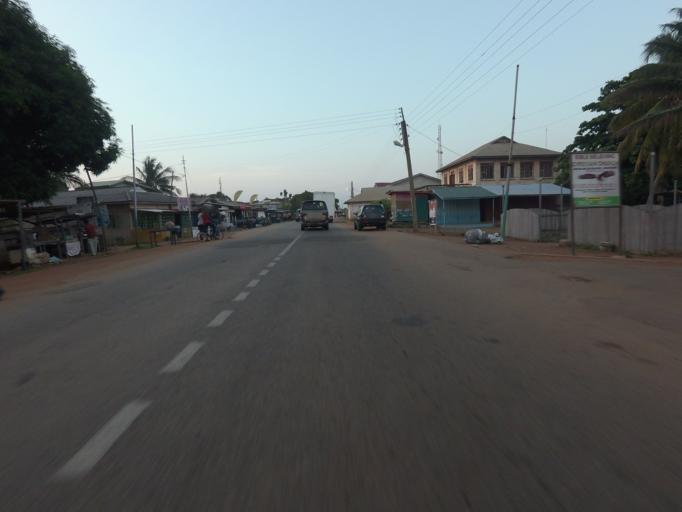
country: GH
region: Volta
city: Keta
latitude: 5.8857
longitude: 0.9826
